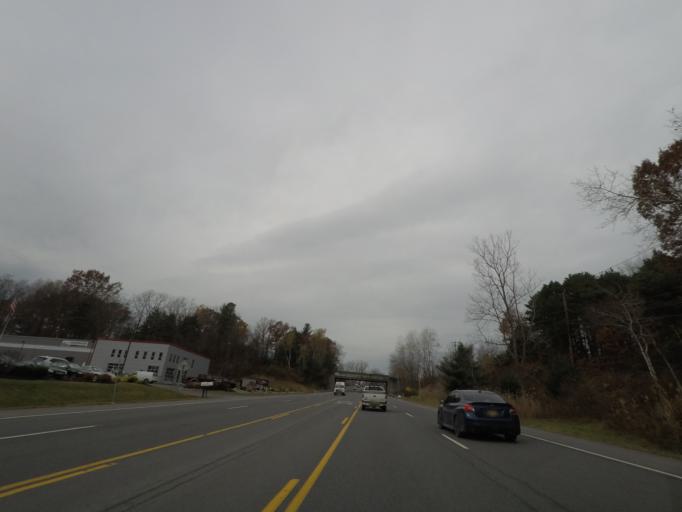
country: US
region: New York
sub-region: Saratoga County
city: Country Knolls
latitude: 42.9033
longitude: -73.7749
